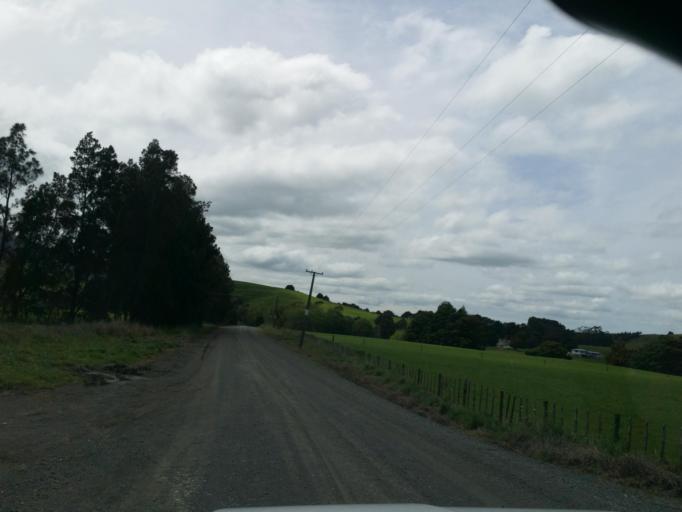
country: NZ
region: Northland
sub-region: Whangarei
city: Maungatapere
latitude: -35.9069
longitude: 174.1318
